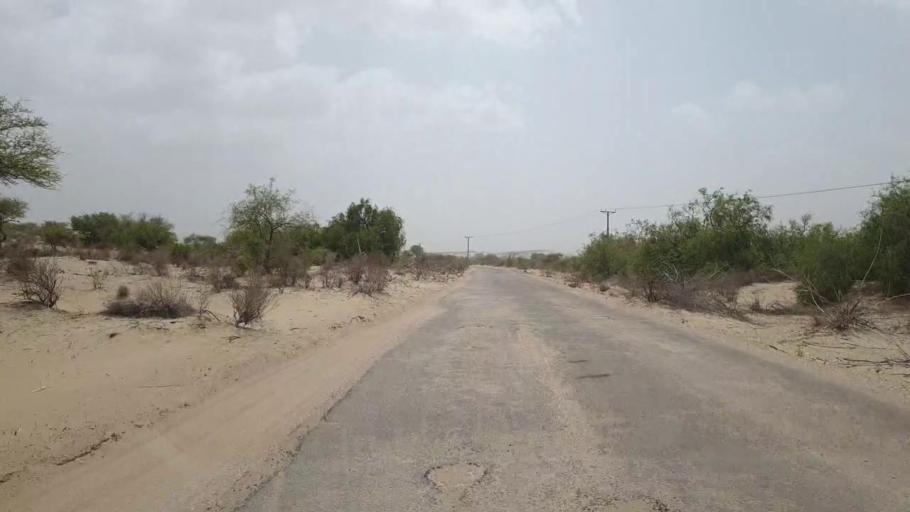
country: PK
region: Sindh
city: Diplo
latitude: 24.3913
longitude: 69.4478
